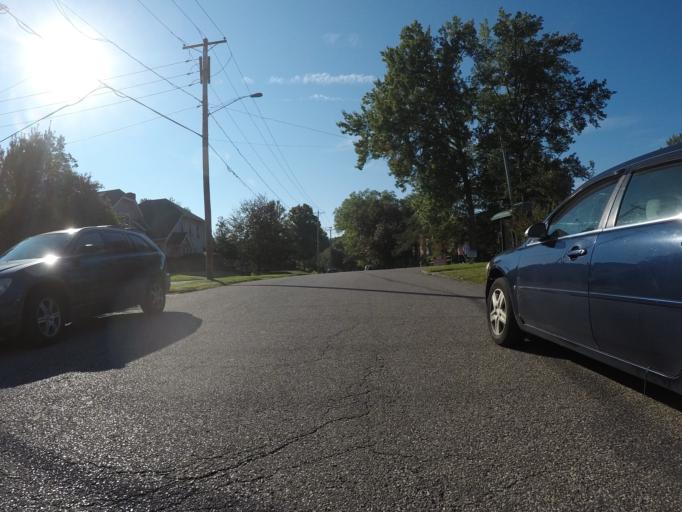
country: US
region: West Virginia
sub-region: Cabell County
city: Huntington
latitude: 38.4109
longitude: -82.4357
